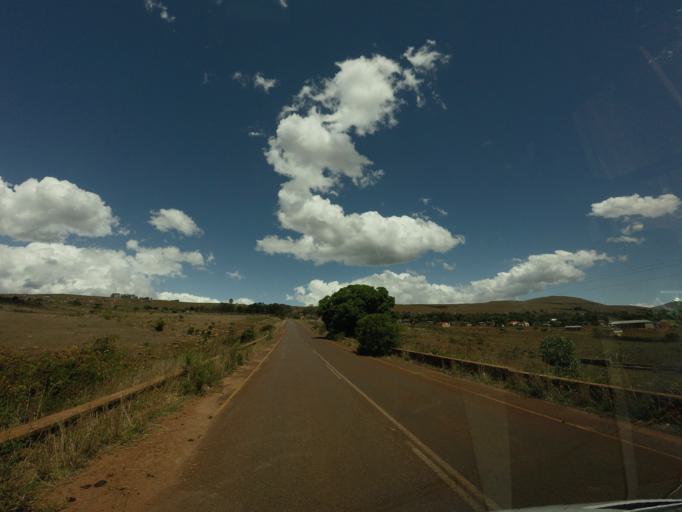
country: ZA
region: Limpopo
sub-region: Mopani District Municipality
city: Hoedspruit
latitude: -24.6103
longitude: 30.7971
